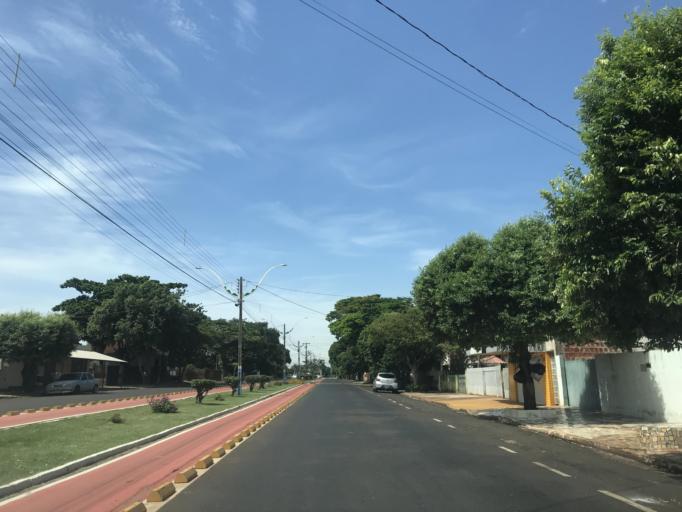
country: BR
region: Parana
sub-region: Terra Rica
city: Terra Rica
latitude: -22.7316
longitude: -52.6246
